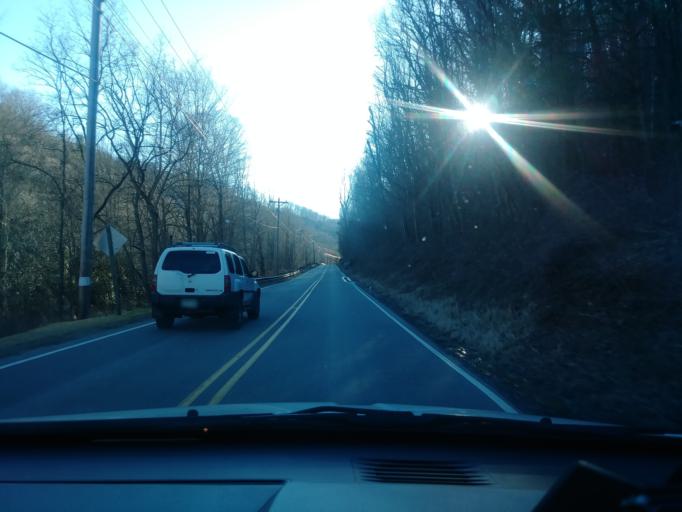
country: US
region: North Carolina
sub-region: Avery County
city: Banner Elk
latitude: 36.1778
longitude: -81.9266
